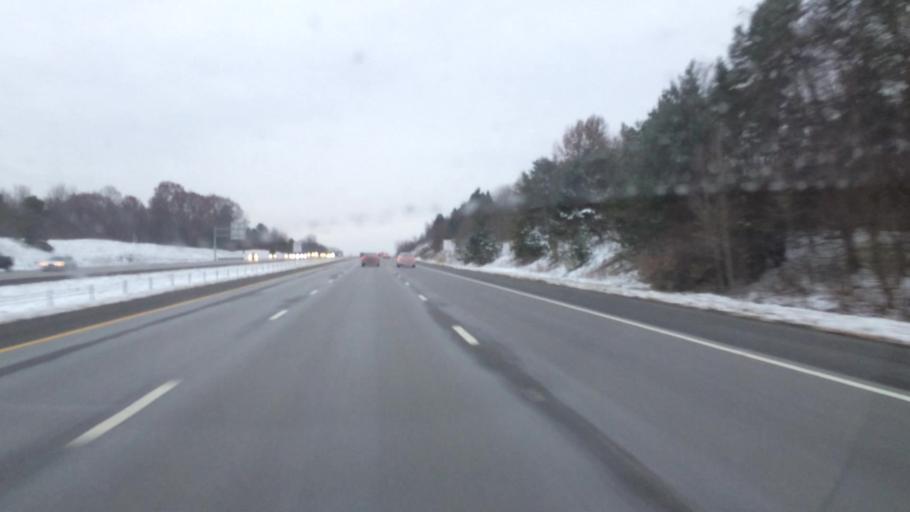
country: US
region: Ohio
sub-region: Medina County
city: Brunswick
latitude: 41.1778
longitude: -81.7877
